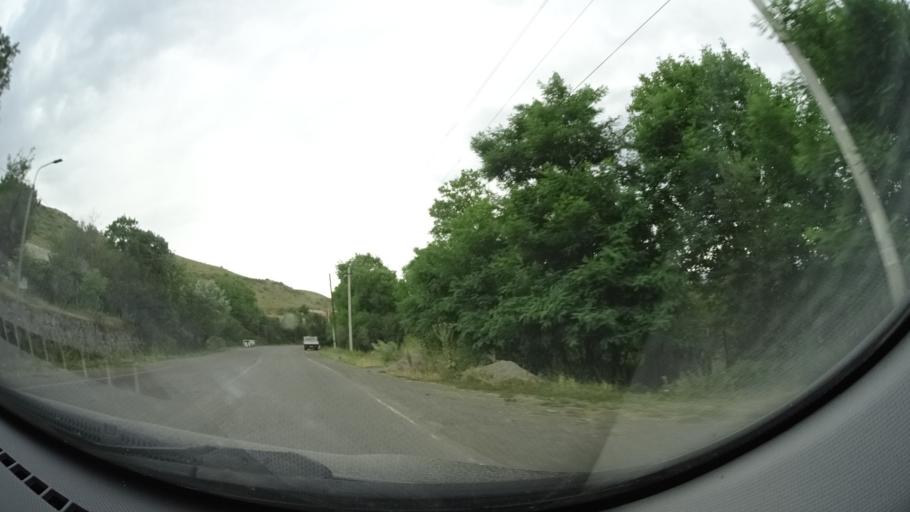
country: GE
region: Samtskhe-Javakheti
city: Akhaltsikhe
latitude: 41.6308
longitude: 43.0459
